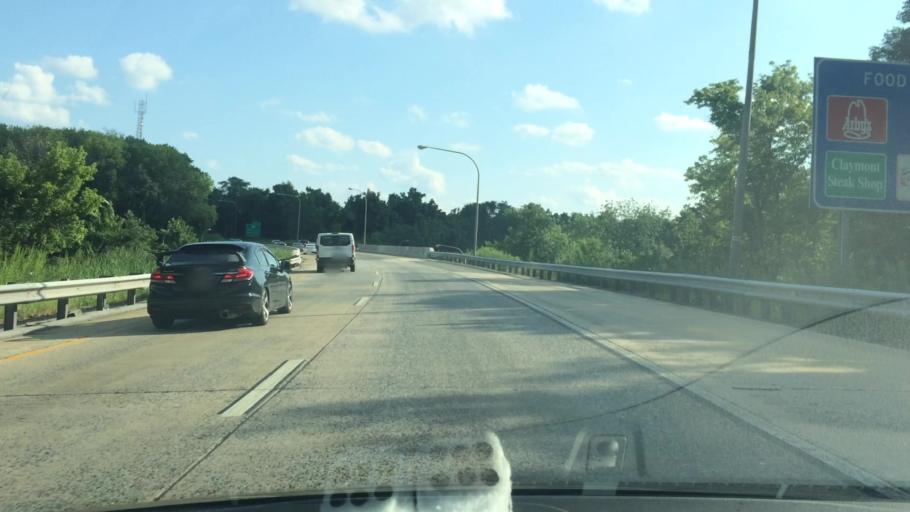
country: US
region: Delaware
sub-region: New Castle County
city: Claymont
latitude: 39.8141
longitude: -75.4554
